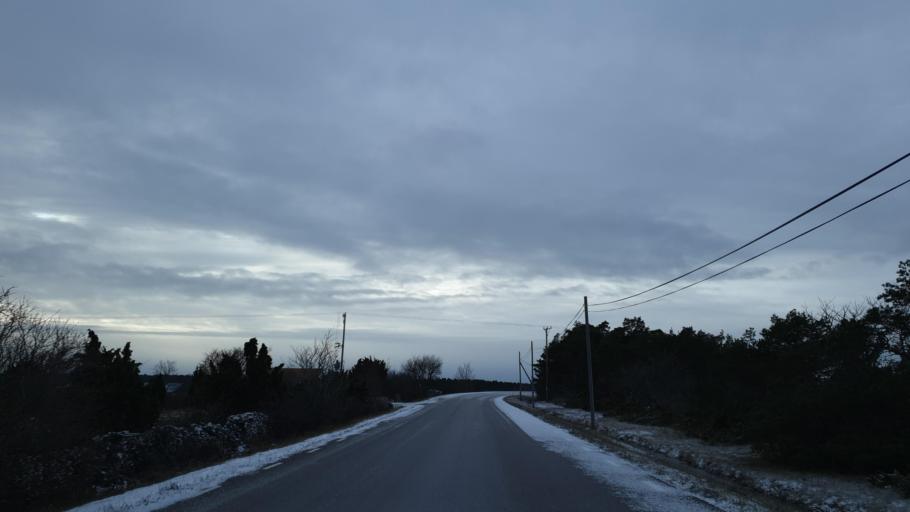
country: SE
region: Gotland
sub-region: Gotland
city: Slite
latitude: 57.4219
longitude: 18.8972
